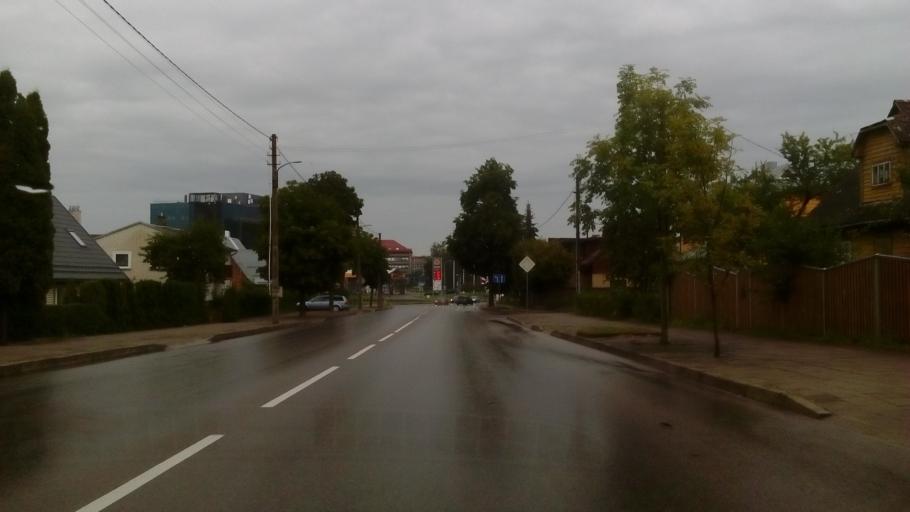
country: LT
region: Alytaus apskritis
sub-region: Alytus
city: Alytus
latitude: 54.3930
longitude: 24.0390
